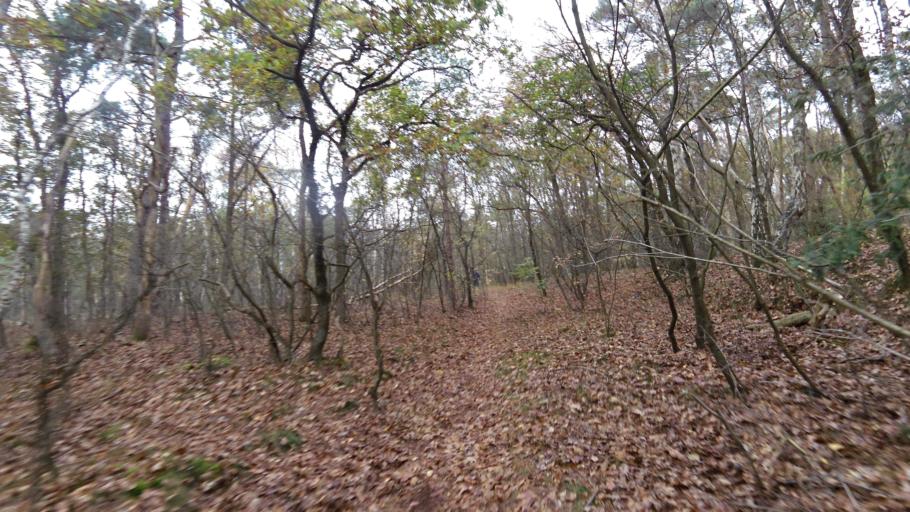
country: NL
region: North Holland
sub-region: Gemeente Hilversum
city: Hilversum
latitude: 52.1950
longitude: 5.1833
